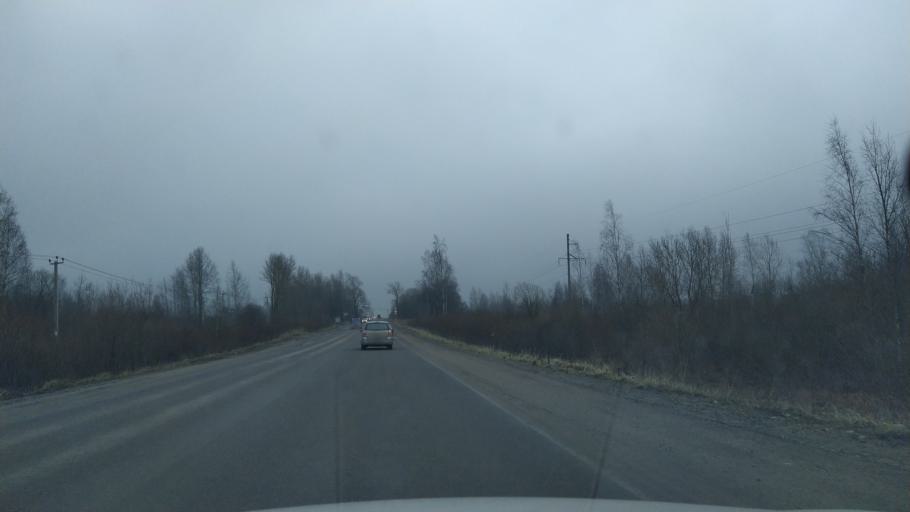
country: RU
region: St.-Petersburg
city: Gorelovo
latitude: 59.7303
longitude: 30.1475
